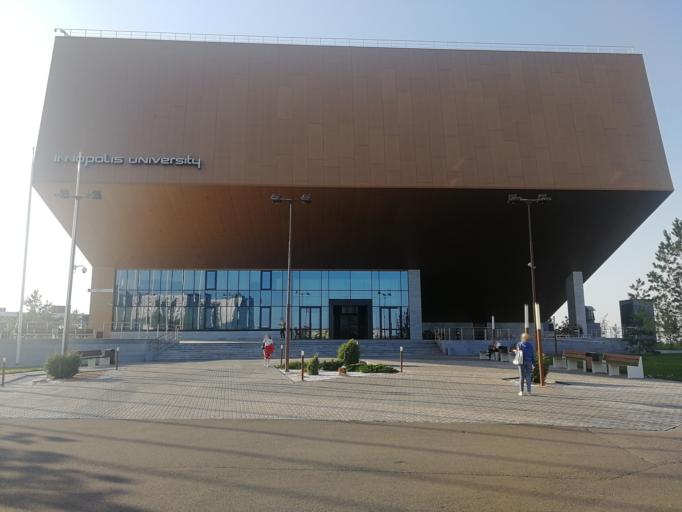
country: RU
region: Tatarstan
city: Sviyazhsk
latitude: 55.7502
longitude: 48.7456
